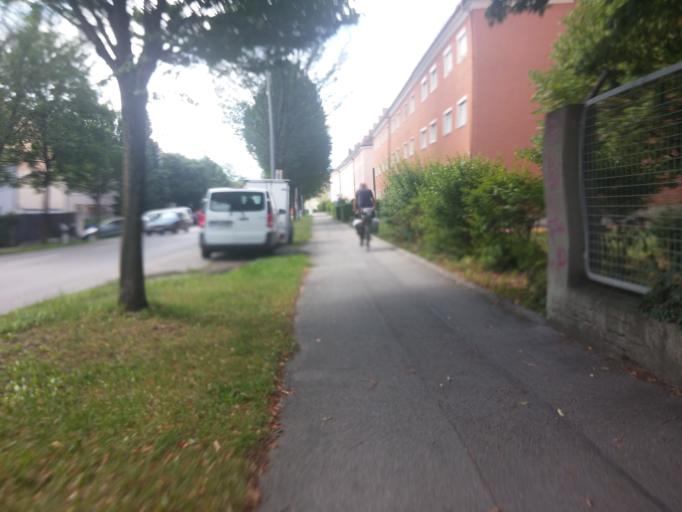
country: DE
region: Bavaria
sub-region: Upper Bavaria
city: Bogenhausen
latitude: 48.1315
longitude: 11.6437
